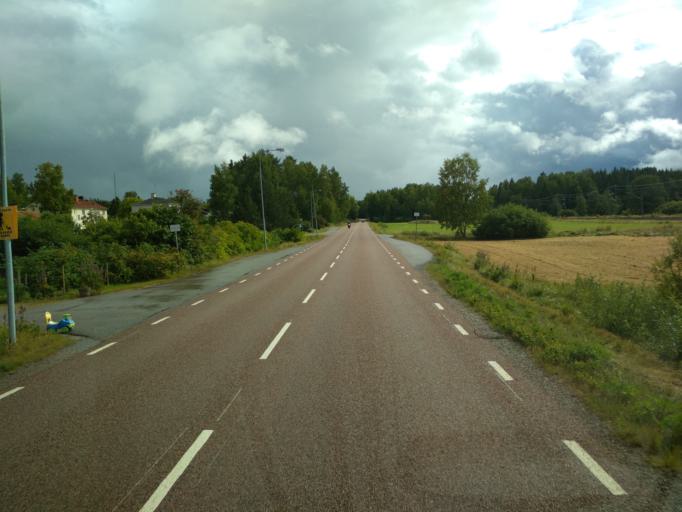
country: SE
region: Vaestmanland
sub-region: Surahammars Kommun
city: Ramnas
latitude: 59.8709
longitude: 16.0854
